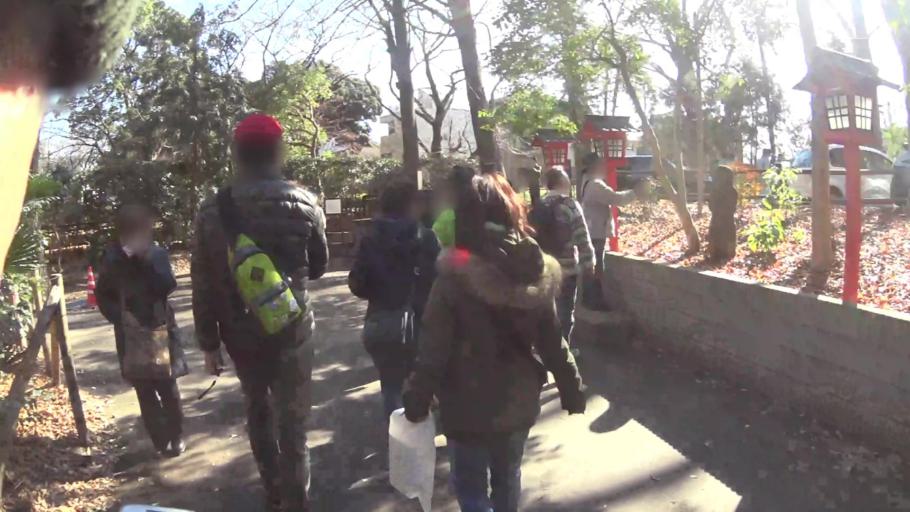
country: JP
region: Saitama
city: Yono
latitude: 35.8533
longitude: 139.6560
